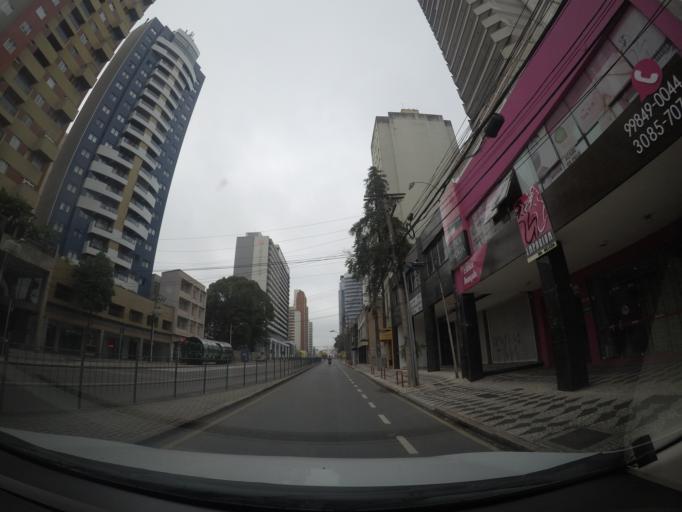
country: BR
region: Parana
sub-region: Curitiba
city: Curitiba
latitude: -25.4149
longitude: -49.2604
